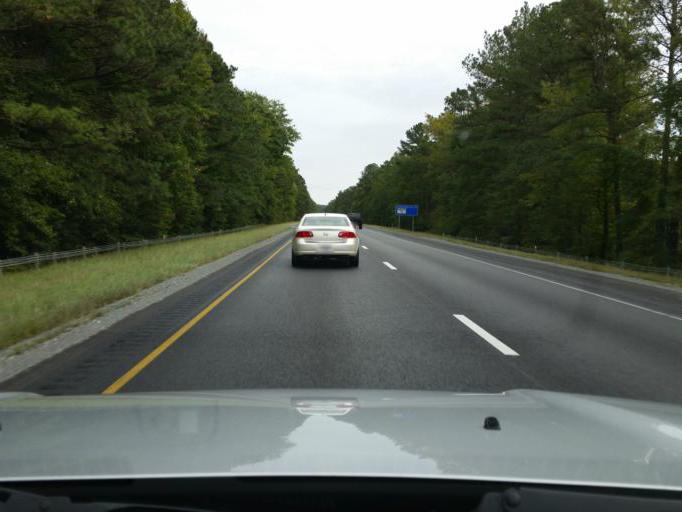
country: US
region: Virginia
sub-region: New Kent County
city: New Kent
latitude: 37.4858
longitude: -76.9552
